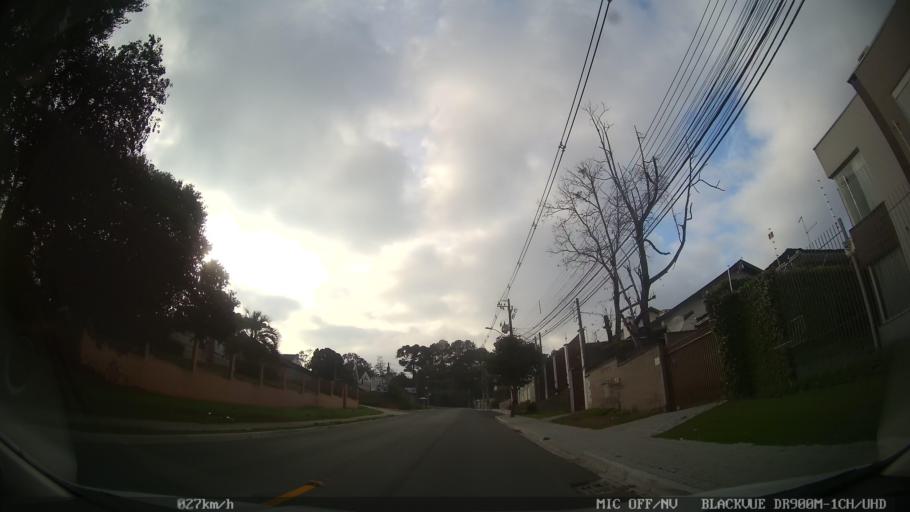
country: BR
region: Parana
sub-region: Curitiba
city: Curitiba
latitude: -25.3992
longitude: -49.3228
